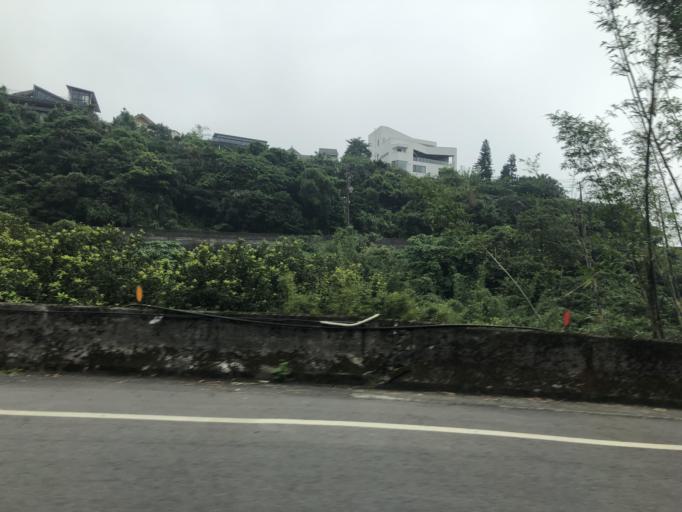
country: TW
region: Taiwan
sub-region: Keelung
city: Keelung
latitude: 25.1888
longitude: 121.6794
